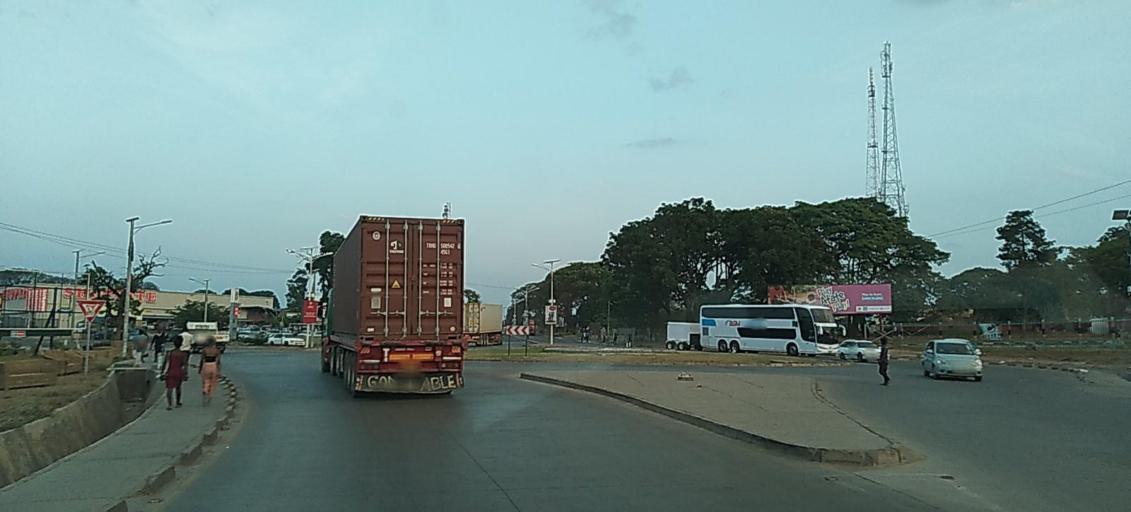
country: ZM
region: Copperbelt
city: Chingola
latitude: -12.5479
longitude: 27.8571
